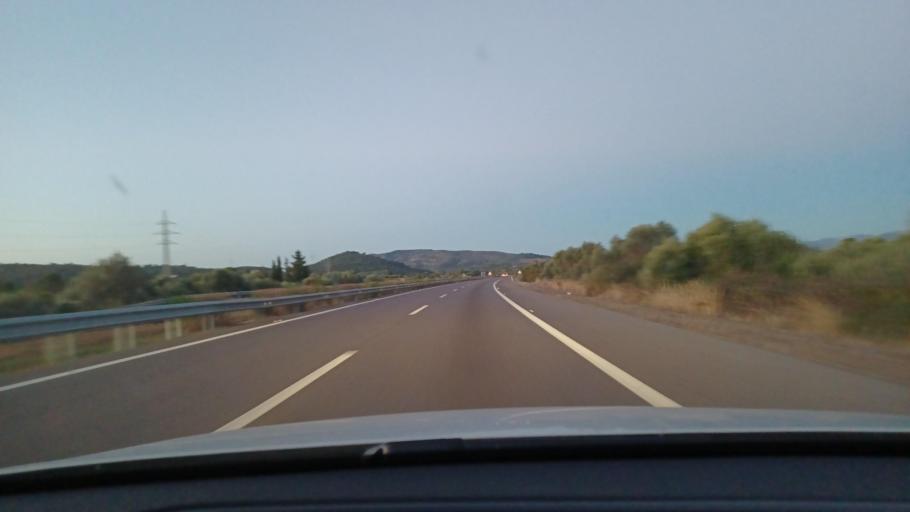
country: ES
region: Catalonia
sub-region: Provincia de Tarragona
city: Masdenverge
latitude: 40.6969
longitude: 0.5391
